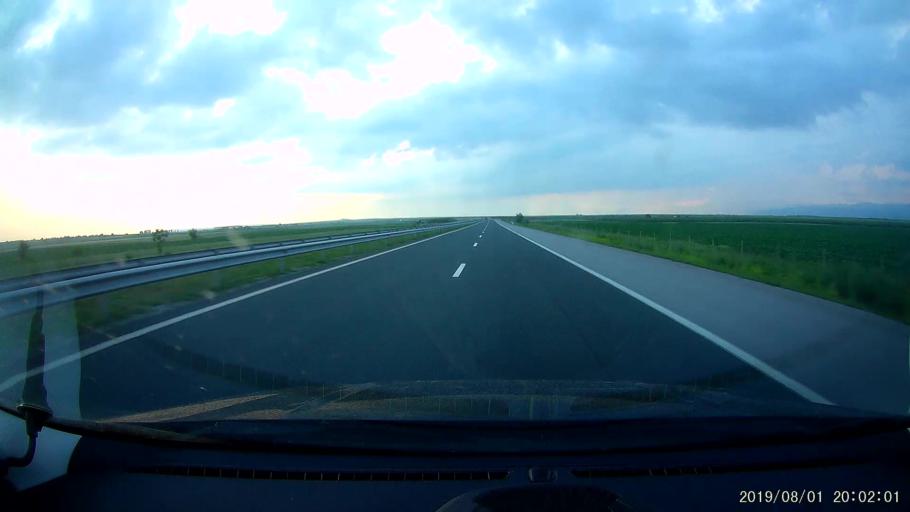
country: BG
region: Yambol
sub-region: Obshtina Straldzha
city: Straldzha
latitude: 42.5579
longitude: 26.6448
